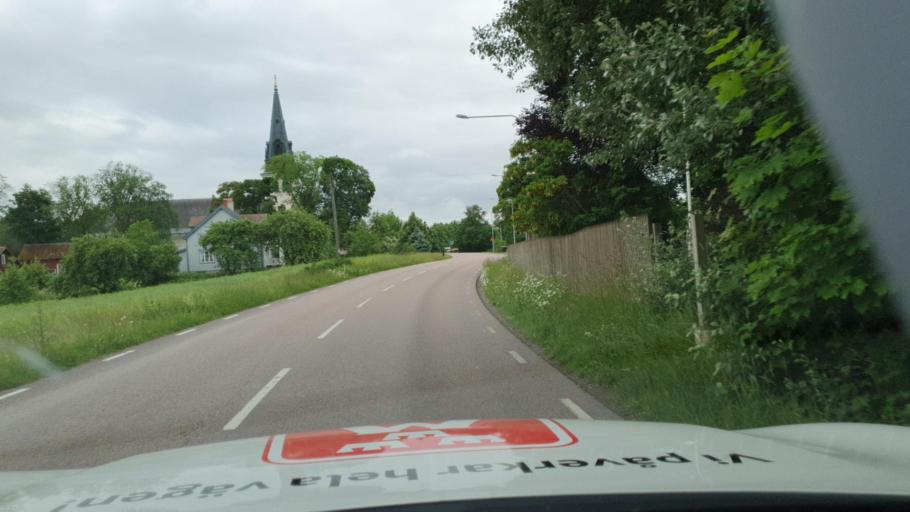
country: SE
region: Vaermland
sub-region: Kils Kommun
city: Kil
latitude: 59.5296
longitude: 13.3155
